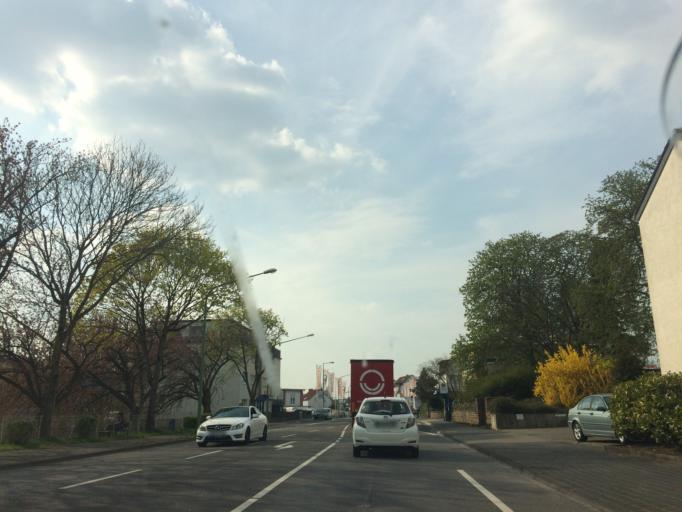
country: DE
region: North Rhine-Westphalia
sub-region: Regierungsbezirk Arnsberg
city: Nachrodt-Wiblingwerde
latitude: 51.3614
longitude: 7.5596
